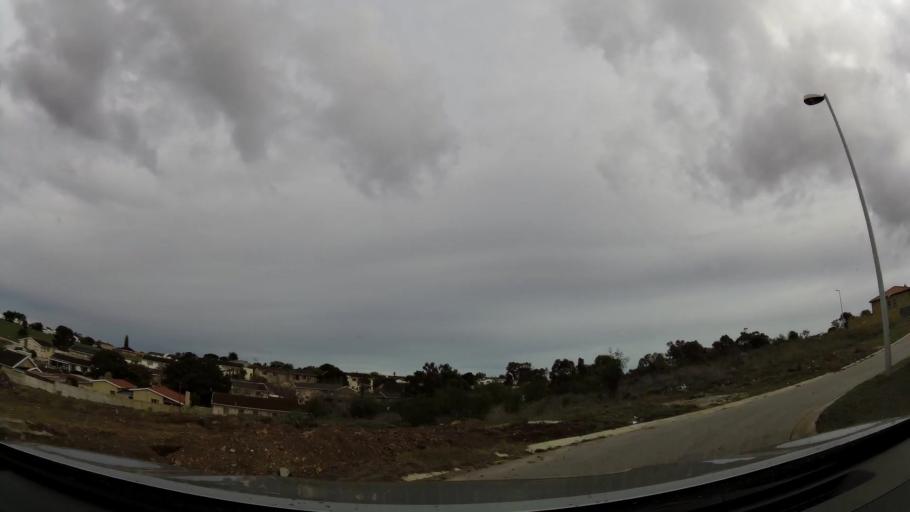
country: ZA
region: Eastern Cape
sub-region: Nelson Mandela Bay Metropolitan Municipality
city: Port Elizabeth
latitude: -33.9299
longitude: 25.5090
